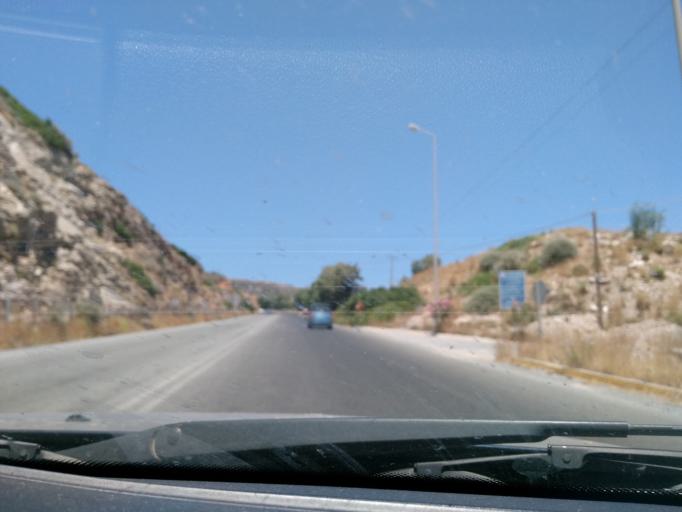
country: GR
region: Crete
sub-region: Nomos Irakleiou
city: Gazi
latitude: 35.3679
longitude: 25.0382
